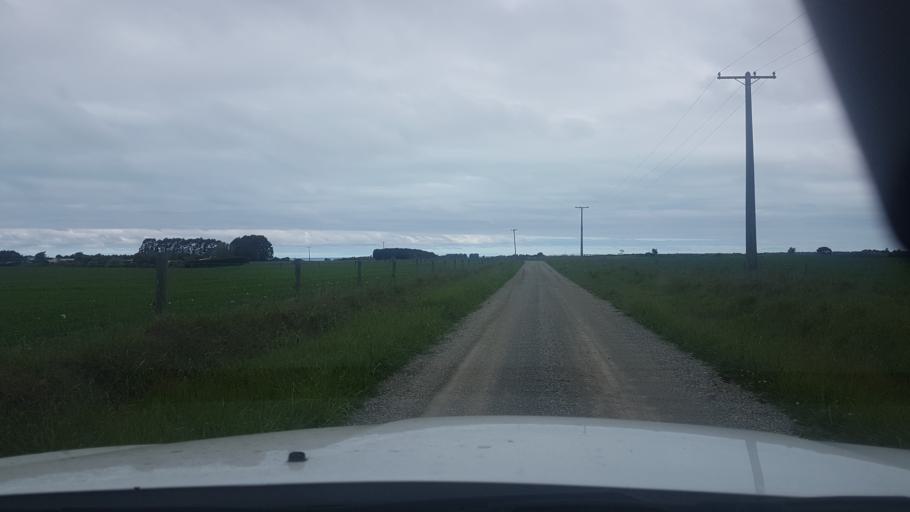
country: NZ
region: Canterbury
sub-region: Timaru District
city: Timaru
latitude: -44.4445
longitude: 171.2060
